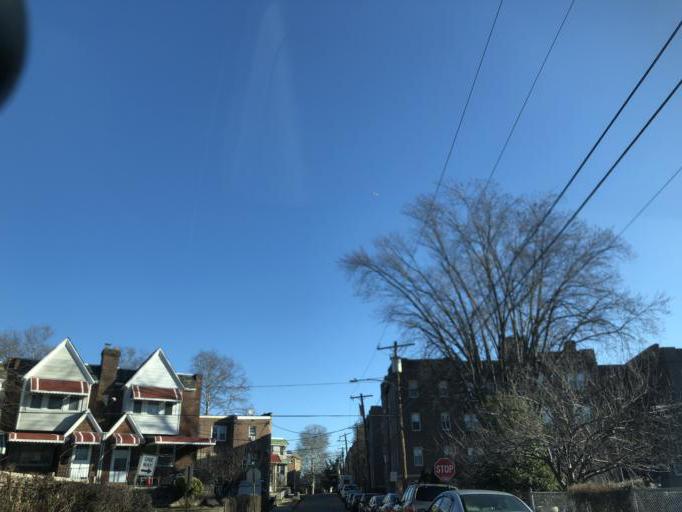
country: US
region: Pennsylvania
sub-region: Delaware County
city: East Lansdowne
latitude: 39.9545
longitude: -75.2669
